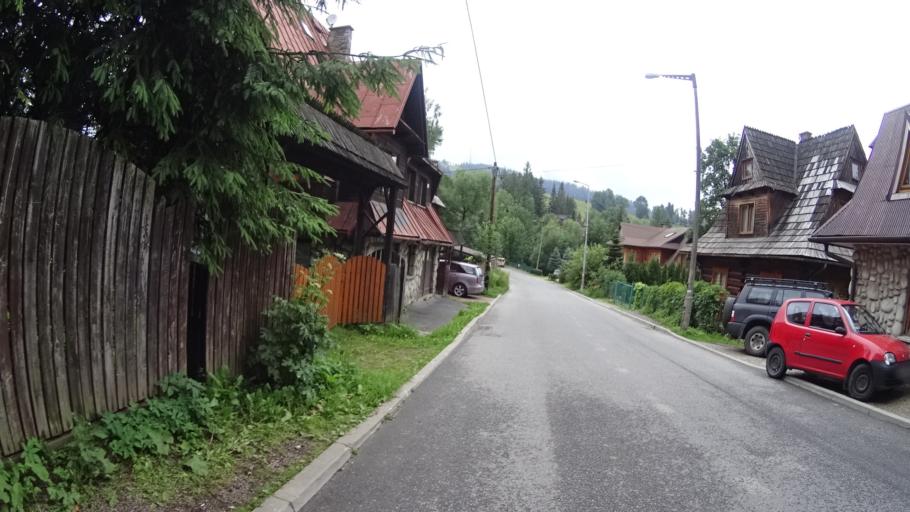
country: PL
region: Lesser Poland Voivodeship
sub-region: Powiat tatrzanski
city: Zakopane
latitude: 49.2922
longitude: 19.9366
